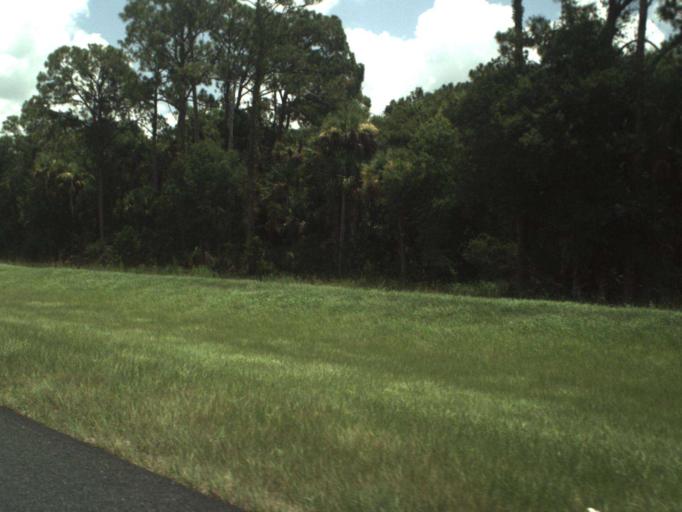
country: US
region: Florida
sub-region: Okeechobee County
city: Taylor Creek
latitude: 27.3349
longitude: -80.6485
